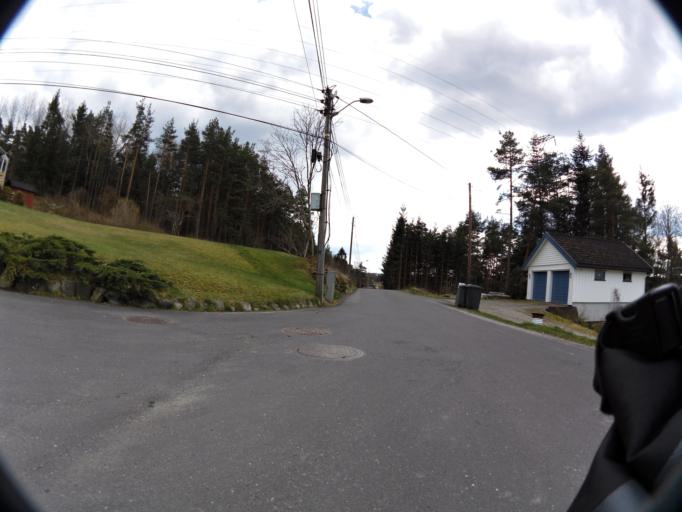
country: NO
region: Ostfold
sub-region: Sarpsborg
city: Sarpsborg
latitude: 59.2781
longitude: 11.0259
